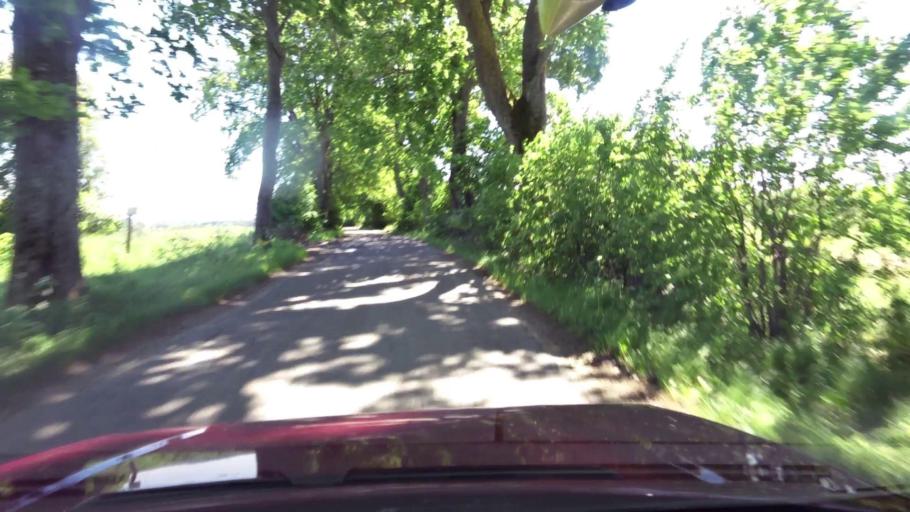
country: PL
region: West Pomeranian Voivodeship
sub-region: Powiat koszalinski
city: Bobolice
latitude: 54.0142
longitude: 16.6545
